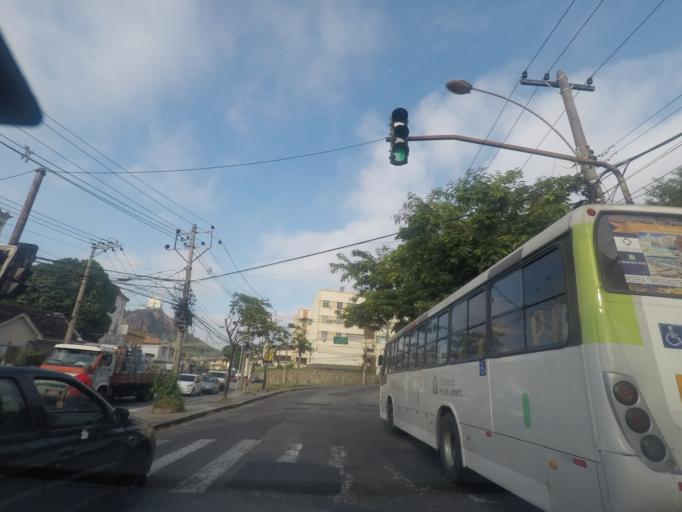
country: BR
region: Rio de Janeiro
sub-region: Duque De Caxias
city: Duque de Caxias
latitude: -22.8420
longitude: -43.2696
